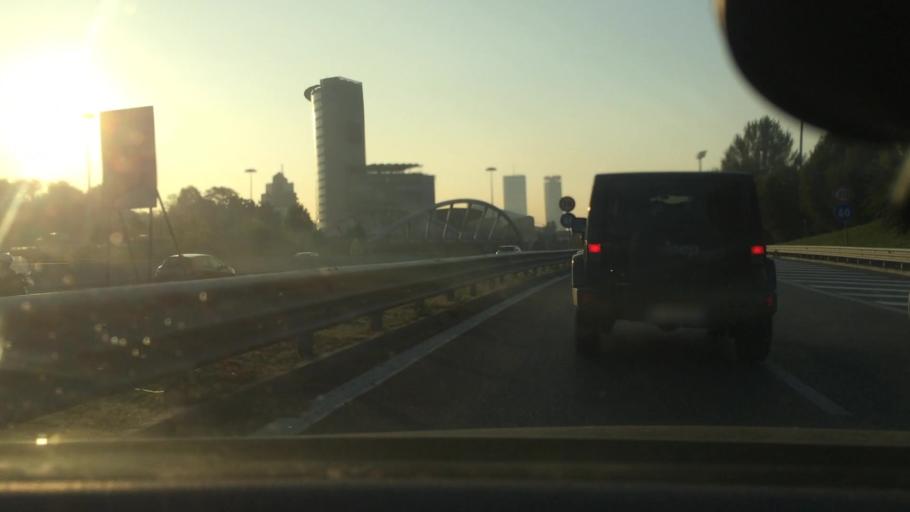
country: IT
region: Lombardy
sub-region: Citta metropolitana di Milano
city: Novate Milanese
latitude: 45.4923
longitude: 9.1365
